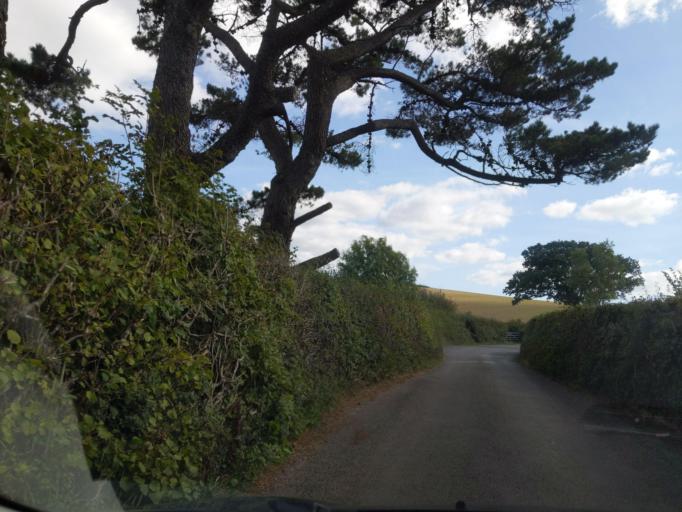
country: GB
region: England
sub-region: Devon
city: Ipplepen
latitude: 50.4615
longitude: -3.6458
